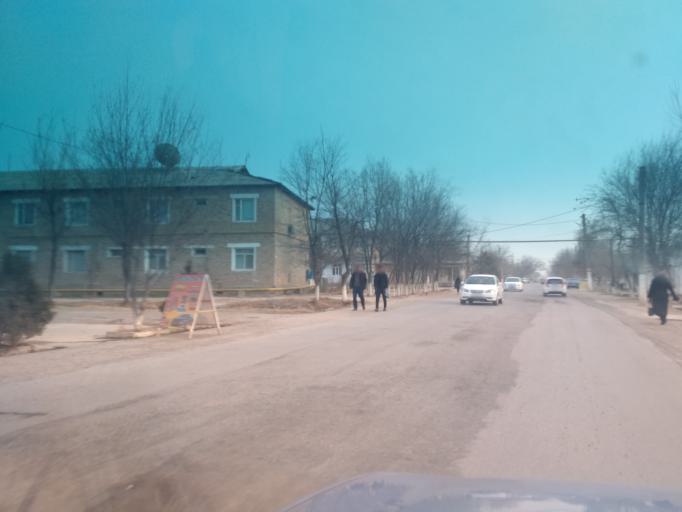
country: UZ
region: Sirdaryo
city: Guliston
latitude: 40.4928
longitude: 68.7871
